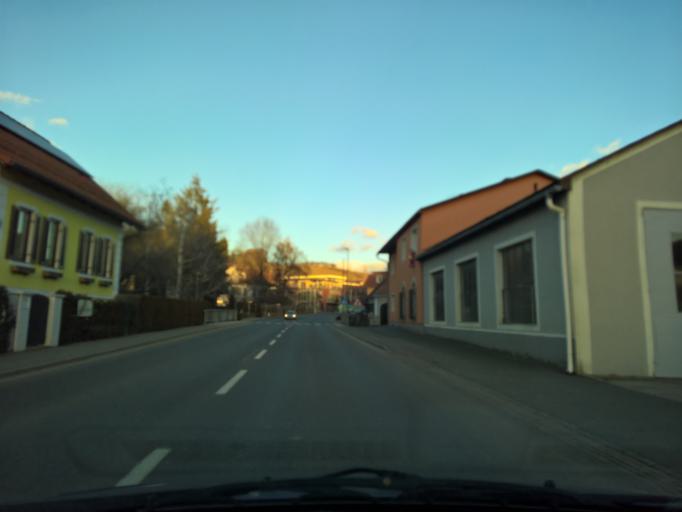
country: AT
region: Styria
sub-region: Politischer Bezirk Leibnitz
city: Gamlitz
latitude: 46.7215
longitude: 15.5581
